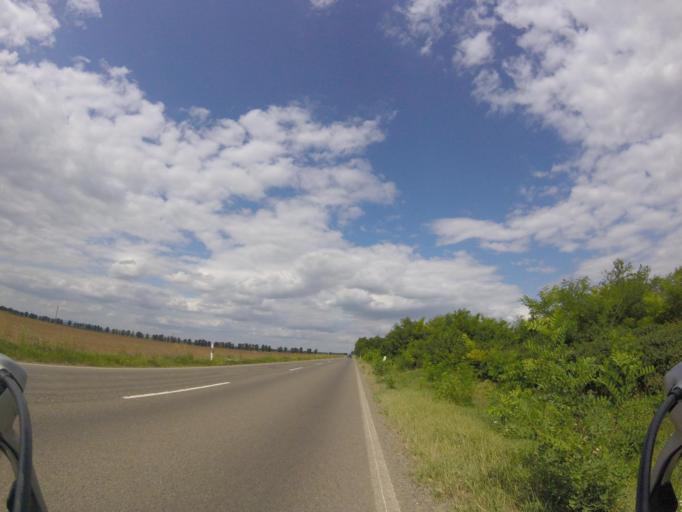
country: HU
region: Baranya
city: Mohacs
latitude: 45.9368
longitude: 18.6625
